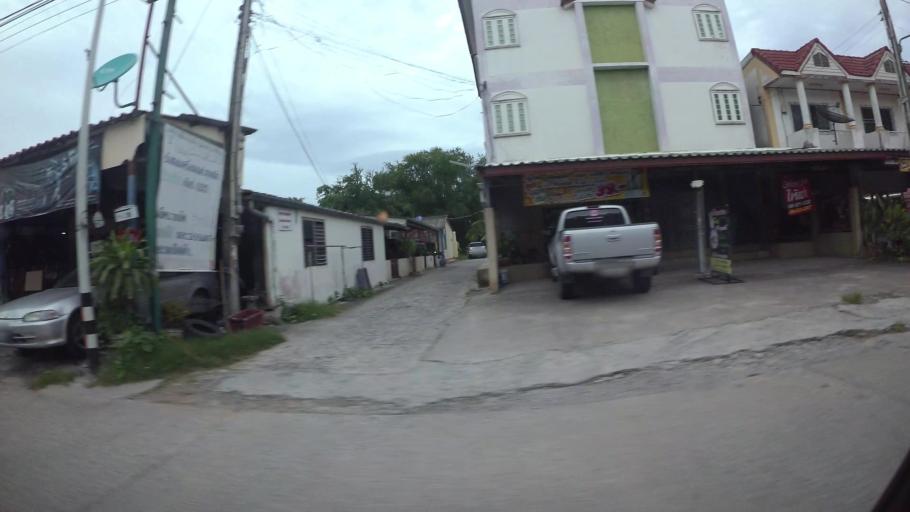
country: TH
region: Chon Buri
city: Si Racha
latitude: 13.1391
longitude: 100.9386
